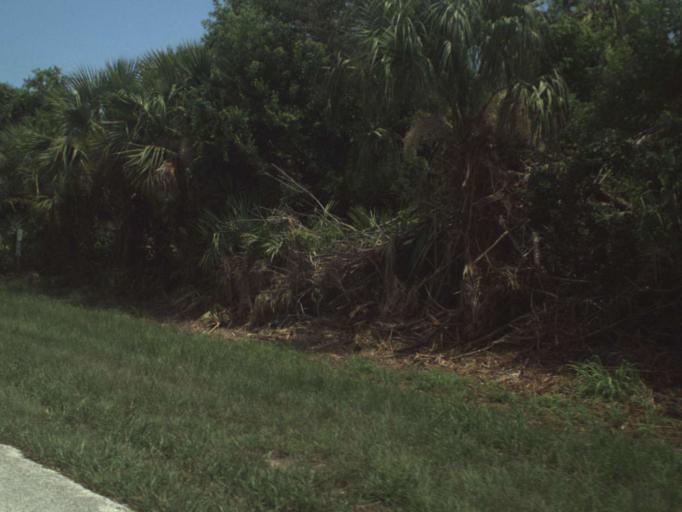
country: US
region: Florida
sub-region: Indian River County
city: Wabasso Beach
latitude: 27.7943
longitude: -80.4146
